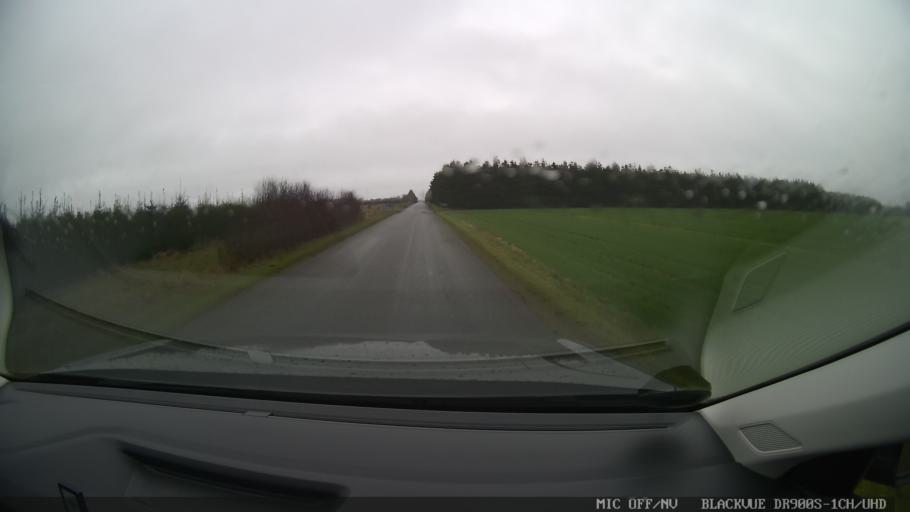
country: DK
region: Central Jutland
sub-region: Viborg Kommune
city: Karup
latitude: 56.2410
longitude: 9.1392
